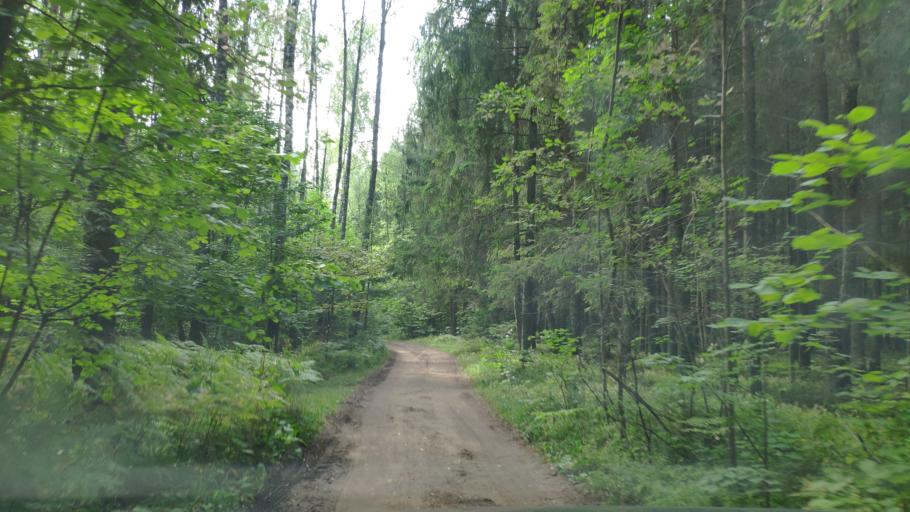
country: BY
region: Minsk
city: Zaslawye
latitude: 53.9646
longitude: 27.2971
